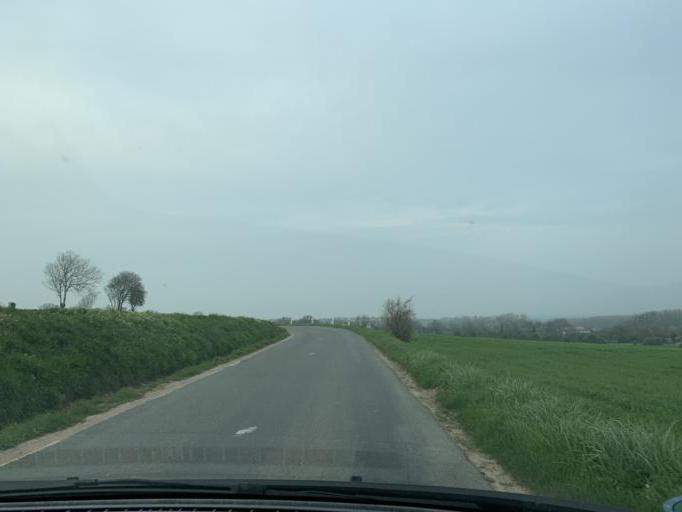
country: FR
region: Nord-Pas-de-Calais
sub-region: Departement du Pas-de-Calais
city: Samer
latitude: 50.6741
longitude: 1.7558
